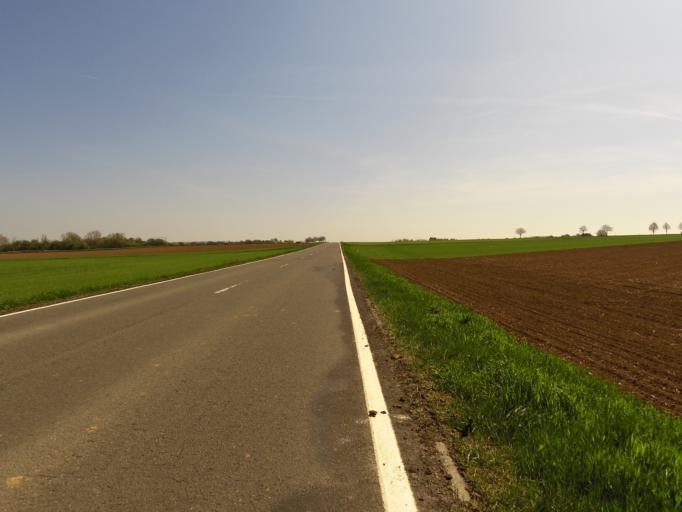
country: DE
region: Rheinland-Pfalz
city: Lautersheim
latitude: 49.5887
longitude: 8.0834
